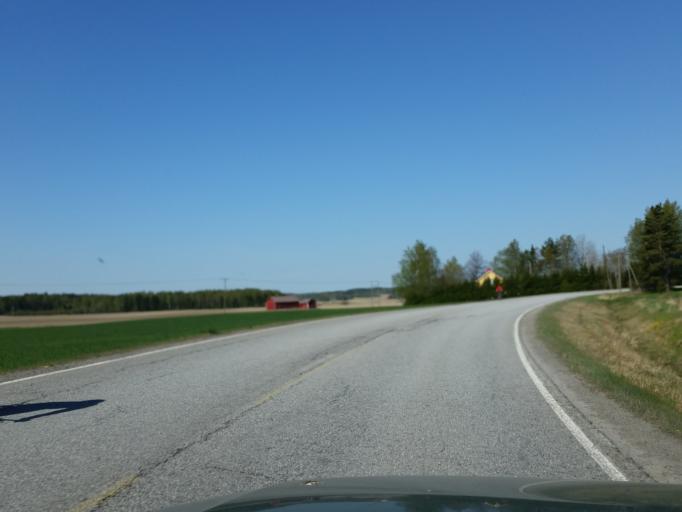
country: FI
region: Uusimaa
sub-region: Helsinki
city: Lohja
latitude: 60.1729
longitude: 24.0986
